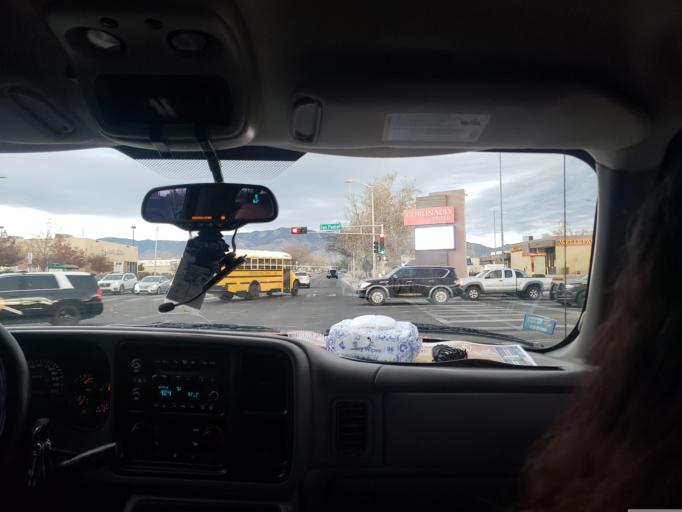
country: US
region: New Mexico
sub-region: Bernalillo County
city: Albuquerque
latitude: 35.1090
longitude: -106.5781
